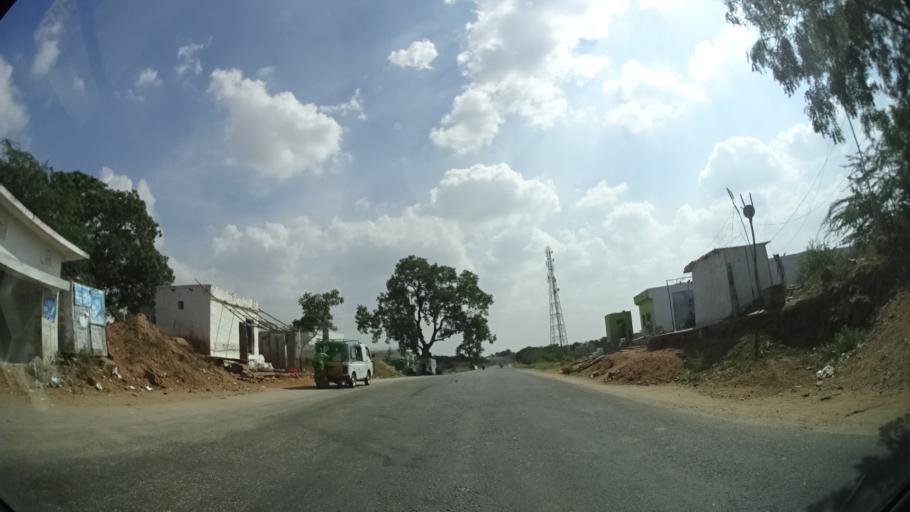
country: IN
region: Andhra Pradesh
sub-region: Anantapur
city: Uravakonda
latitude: 14.8246
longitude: 77.3424
